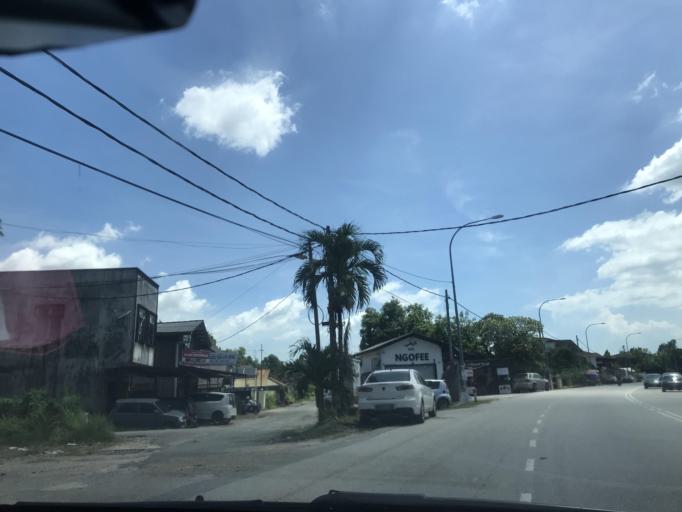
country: MY
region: Kelantan
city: Kota Bharu
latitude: 6.1109
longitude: 102.2635
